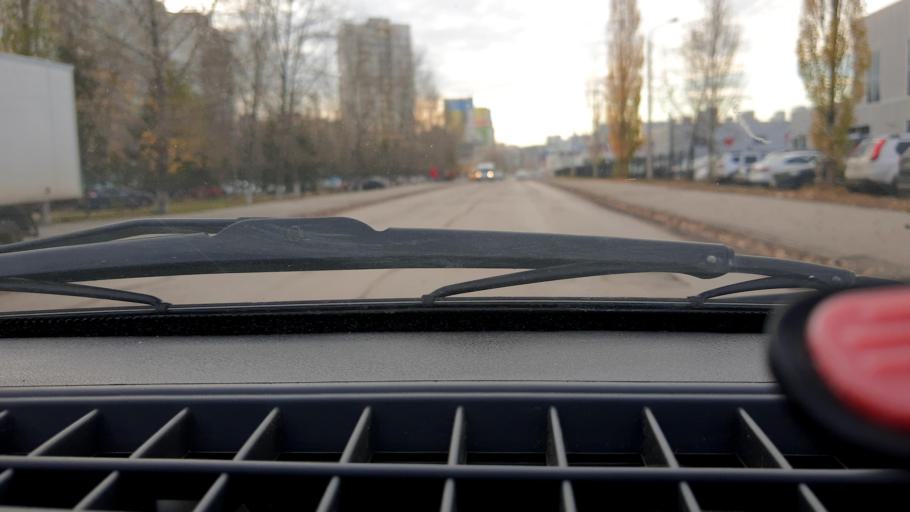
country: RU
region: Bashkortostan
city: Ufa
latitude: 54.7734
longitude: 56.0672
